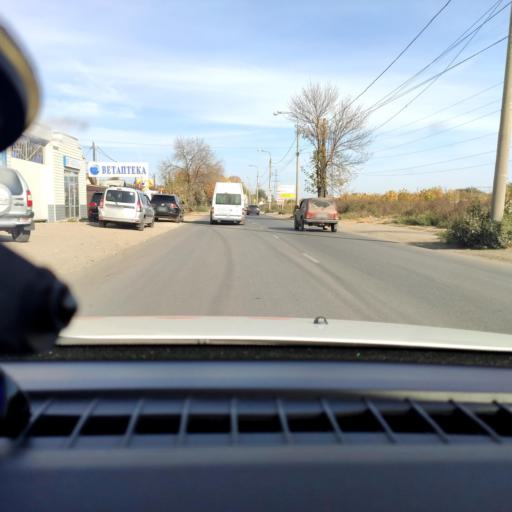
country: RU
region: Samara
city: Smyshlyayevka
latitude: 53.2276
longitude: 50.3022
